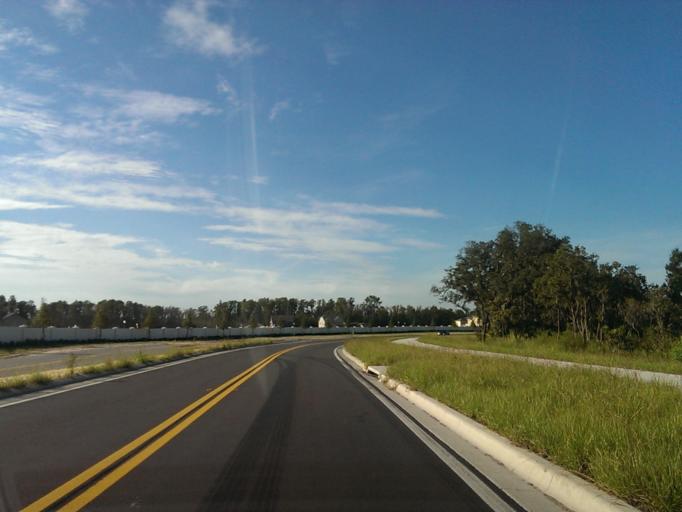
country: US
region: Florida
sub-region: Orange County
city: Lake Butler
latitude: 28.4339
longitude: -81.6052
